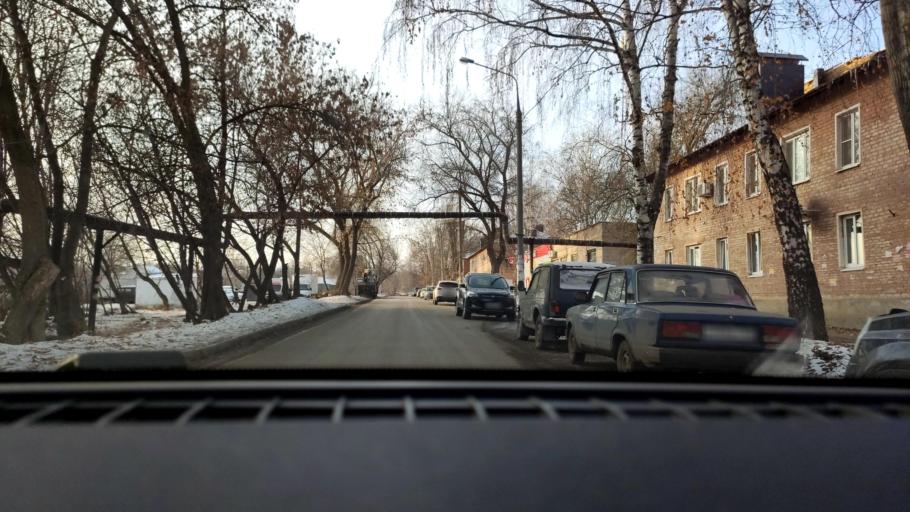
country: RU
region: Samara
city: Petra-Dubrava
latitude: 53.3014
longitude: 50.2748
